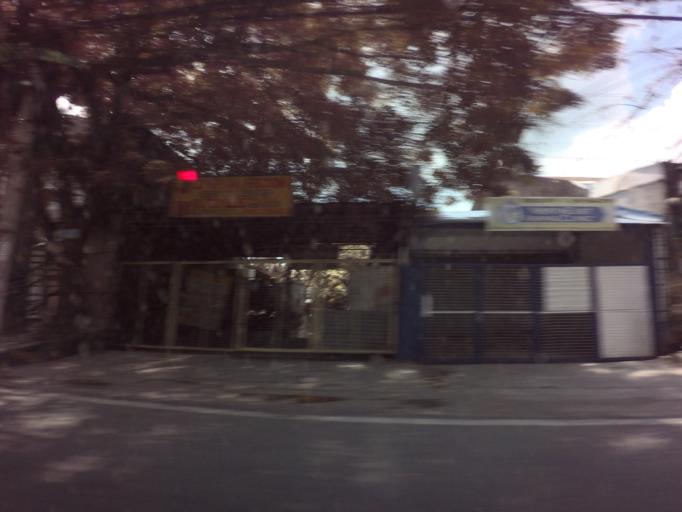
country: PH
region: Calabarzon
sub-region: Province of Laguna
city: San Pedro
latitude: 14.4026
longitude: 121.0473
